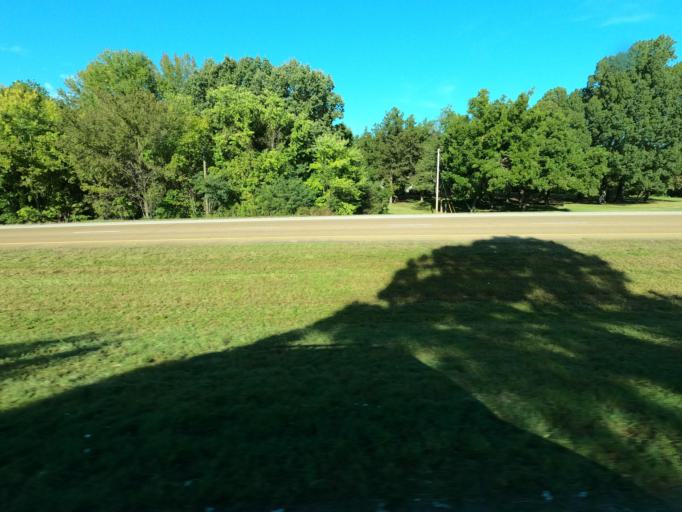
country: US
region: Tennessee
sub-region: Shelby County
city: Millington
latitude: 35.3916
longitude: -89.8545
